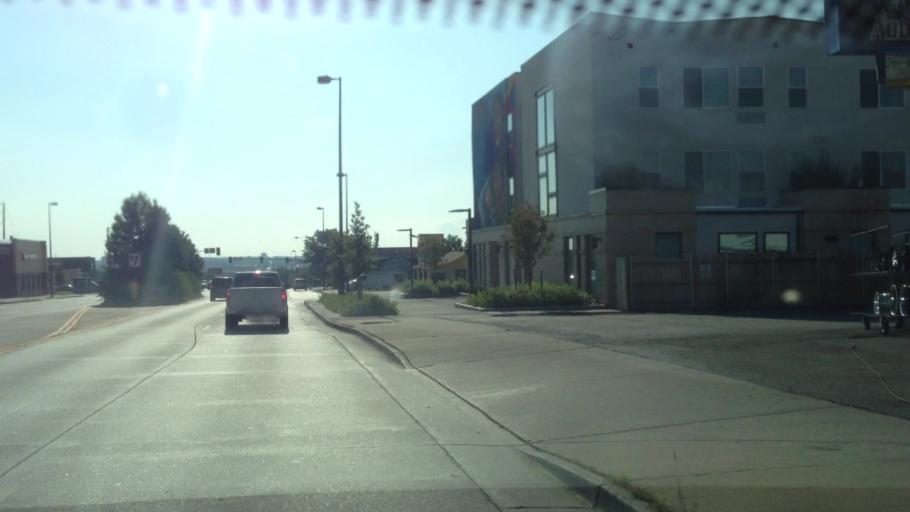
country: US
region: Colorado
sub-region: Denver County
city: Denver
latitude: 39.7111
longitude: -105.0274
